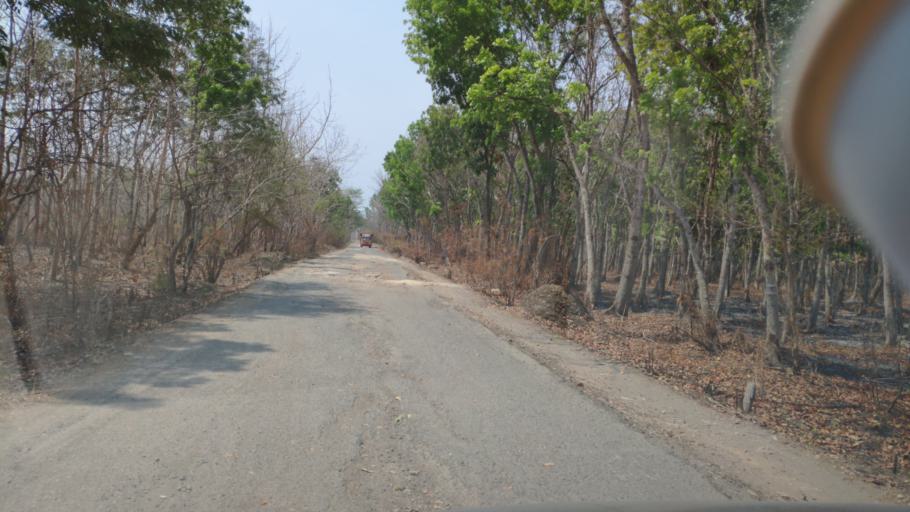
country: ID
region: Central Java
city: Pipes
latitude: -7.1309
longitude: 111.2603
